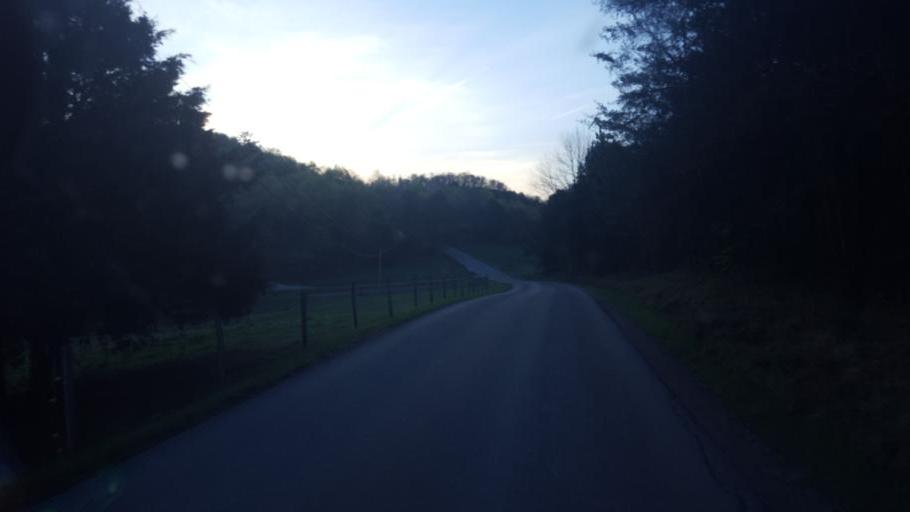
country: US
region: Kentucky
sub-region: Hart County
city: Munfordville
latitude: 37.2677
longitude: -85.9566
